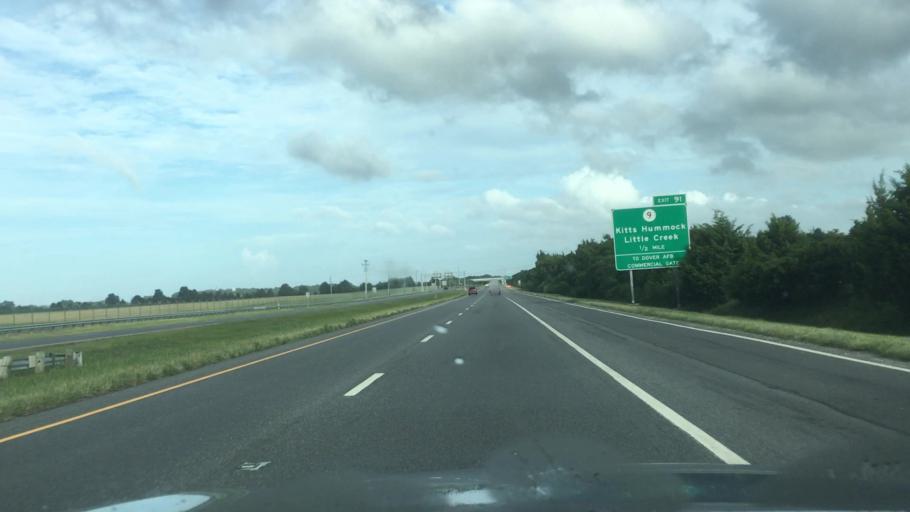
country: US
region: Delaware
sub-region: Kent County
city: Dover Base Housing
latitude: 39.1122
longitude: -75.4647
